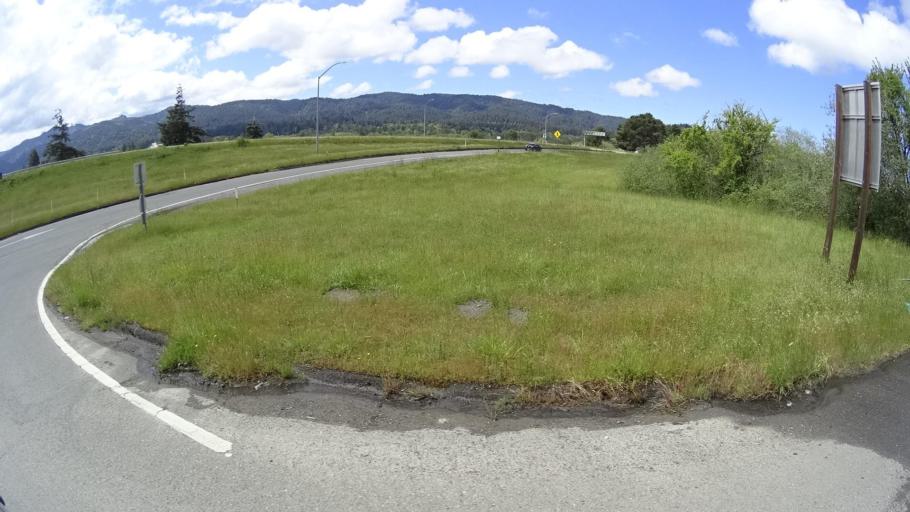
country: US
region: California
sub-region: Humboldt County
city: Blue Lake
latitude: 40.8889
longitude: -123.9982
